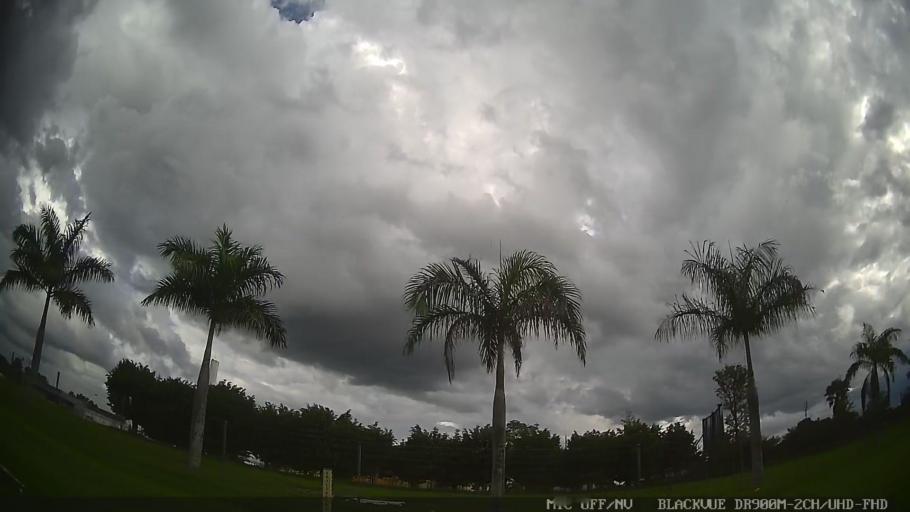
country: BR
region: Sao Paulo
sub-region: Jaguariuna
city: Jaguariuna
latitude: -22.6810
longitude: -47.0062
